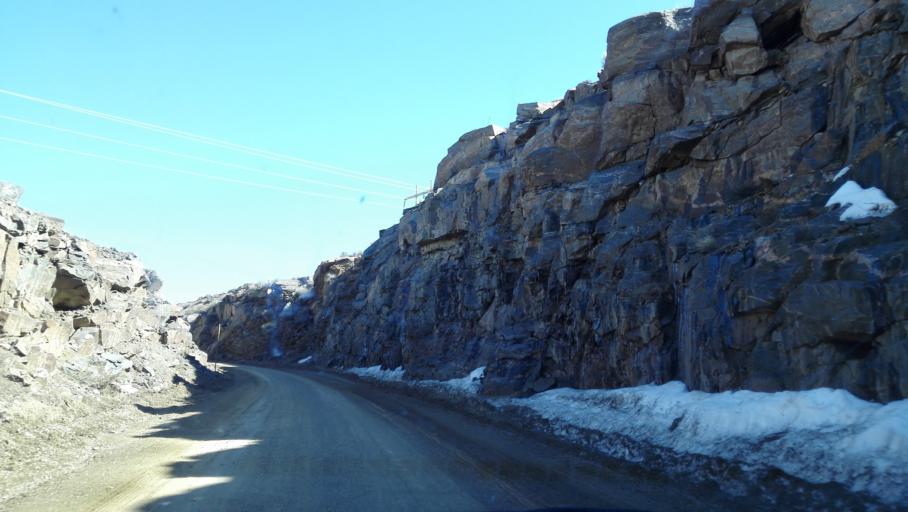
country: US
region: Colorado
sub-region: Hinsdale County
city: Lake City
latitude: 38.4458
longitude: -107.3428
